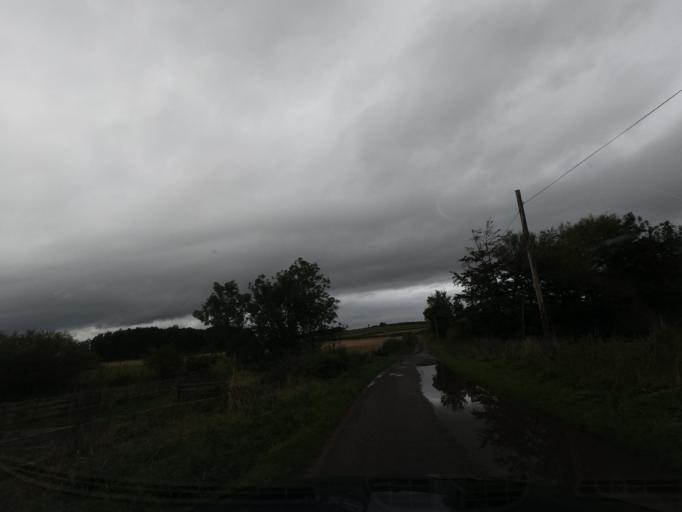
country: GB
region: England
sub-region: Northumberland
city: Ford
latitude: 55.5999
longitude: -2.0479
